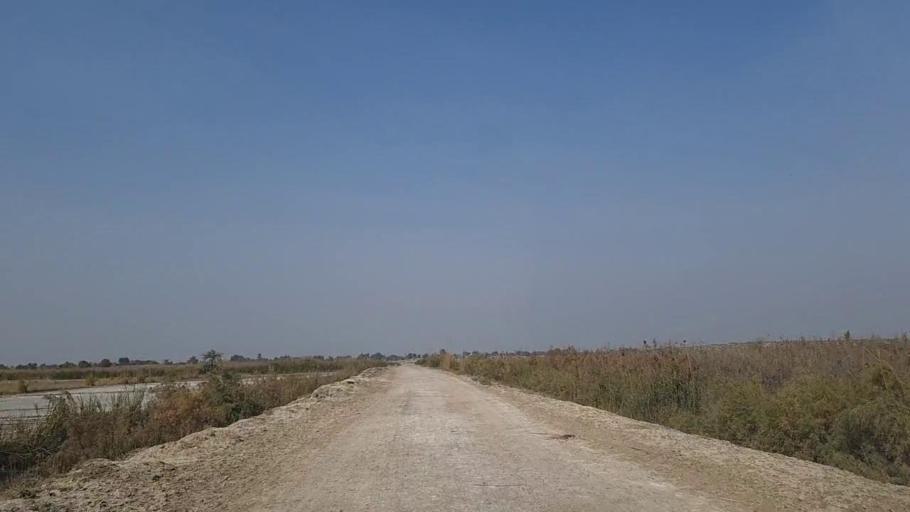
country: PK
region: Sindh
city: Daur
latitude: 26.5050
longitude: 68.4796
